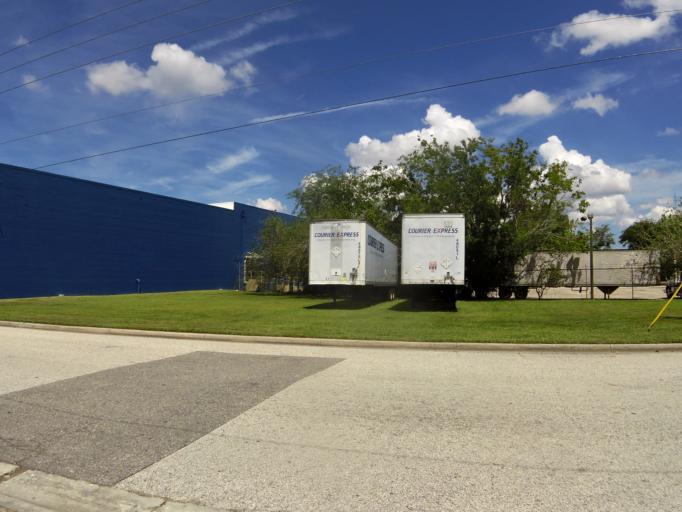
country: US
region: Florida
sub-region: Duval County
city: Jacksonville
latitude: 30.3353
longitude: -81.6381
